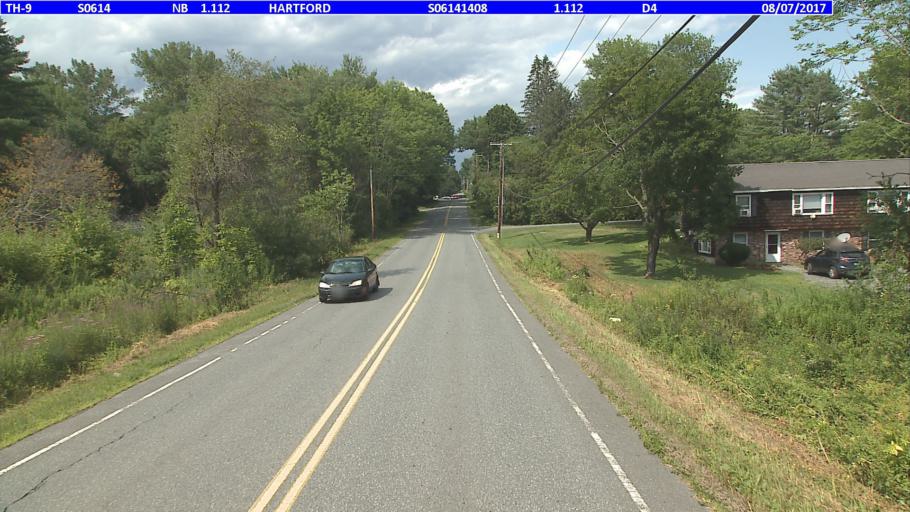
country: US
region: Vermont
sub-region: Windsor County
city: Wilder
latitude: 43.6702
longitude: -72.3253
